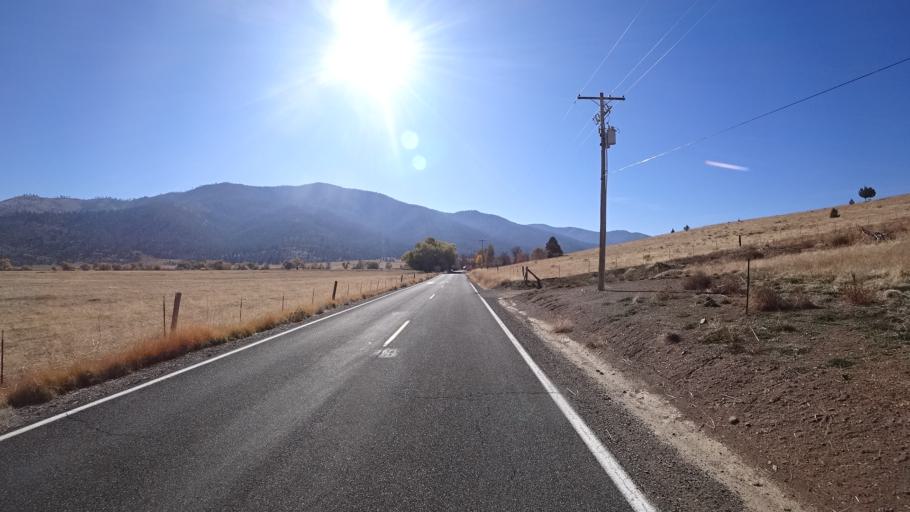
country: US
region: California
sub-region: Siskiyou County
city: Weed
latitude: 41.4968
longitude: -122.5511
